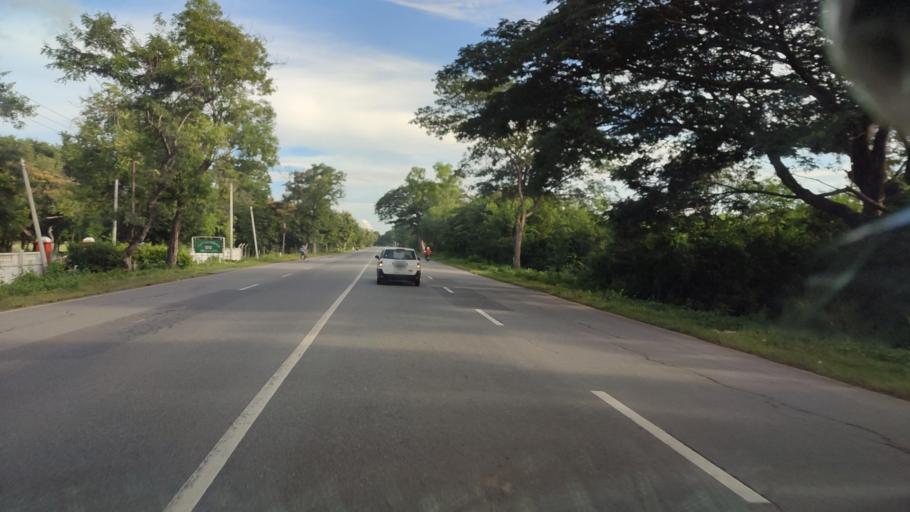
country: MM
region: Mandalay
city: Yamethin
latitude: 20.1567
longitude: 96.1914
